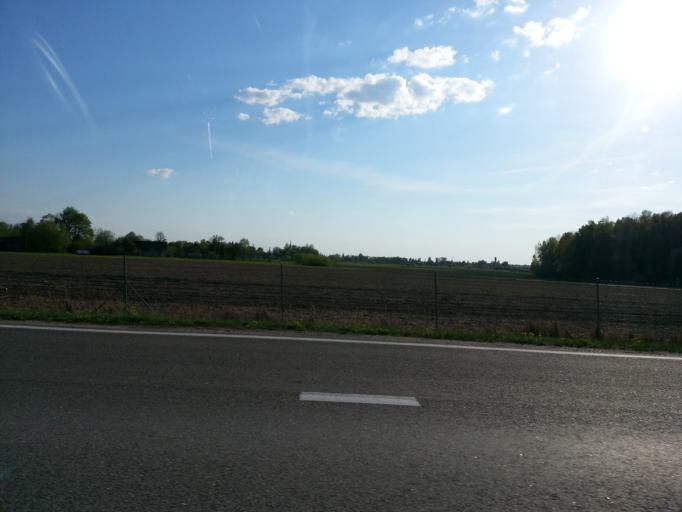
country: LT
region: Vilnius County
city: Ukmerge
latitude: 55.5001
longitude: 24.6181
